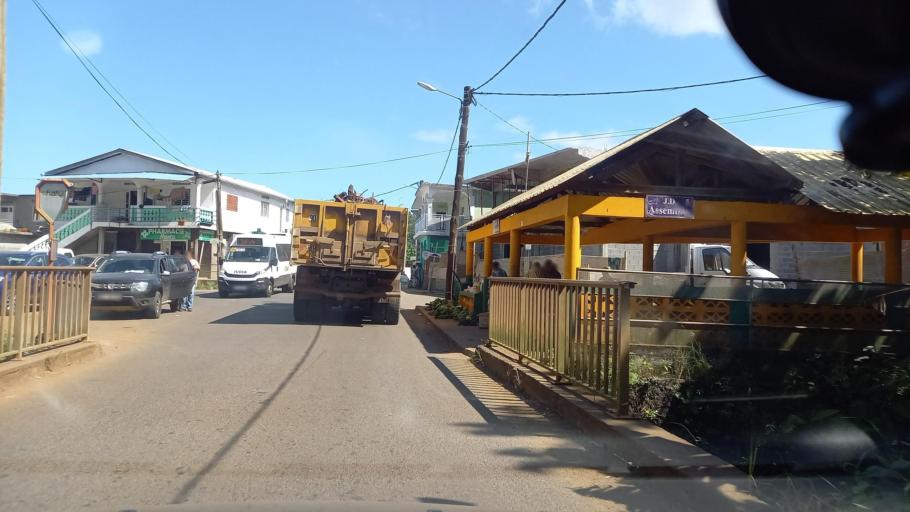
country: YT
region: M'Tsangamouji
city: M'Tsangamouji
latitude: -12.7610
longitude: 45.0875
